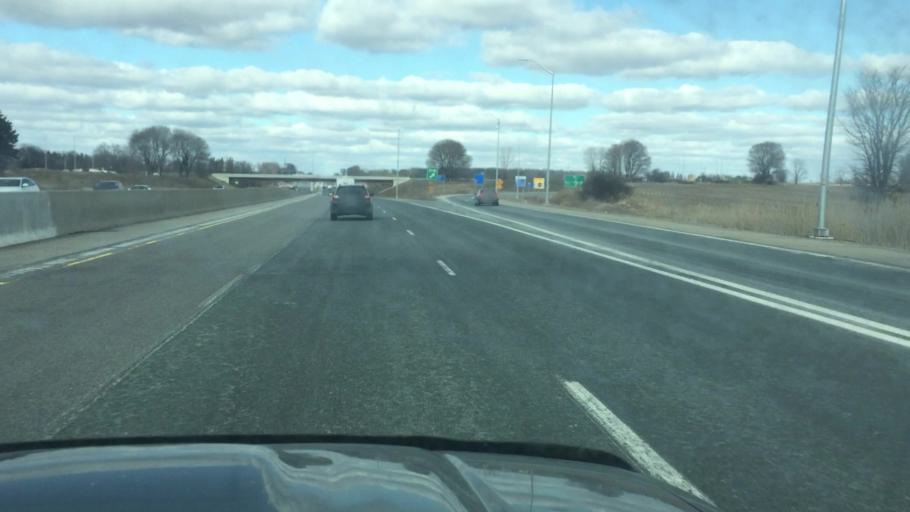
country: CA
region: Ontario
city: Ingersoll
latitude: 43.0247
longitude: -80.8579
